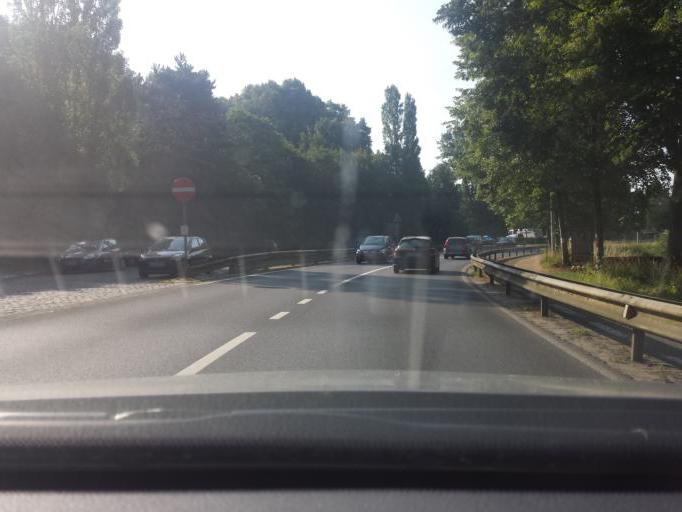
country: BE
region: Flanders
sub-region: Provincie Vlaams-Brabant
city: Diest
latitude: 50.9883
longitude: 5.0622
